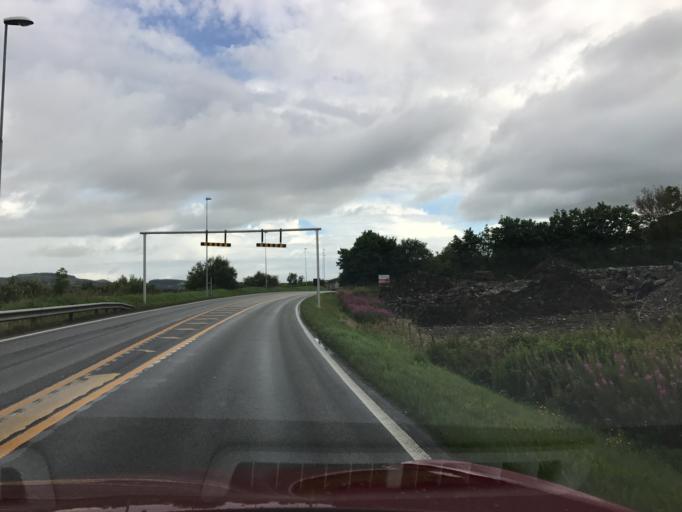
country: NO
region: Rogaland
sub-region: Rennesoy
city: Vikevag
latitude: 59.0692
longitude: 5.6732
